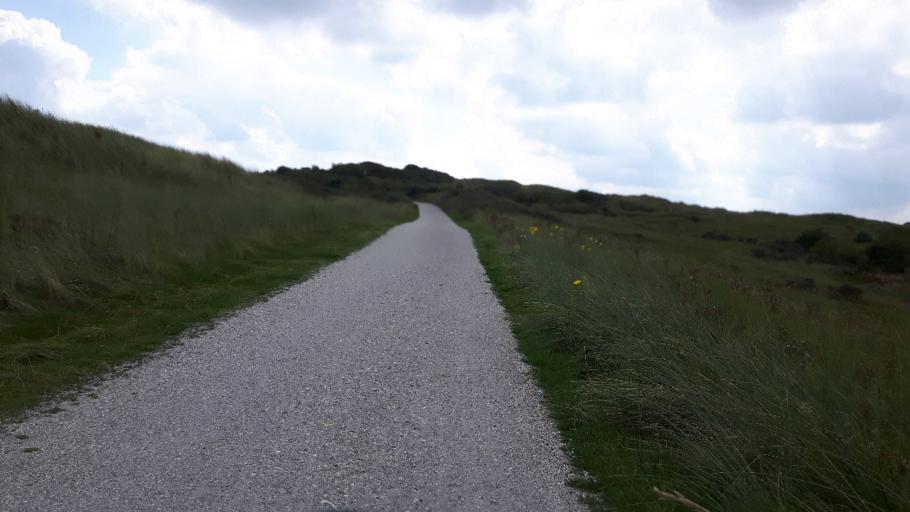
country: NL
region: Friesland
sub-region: Gemeente Dongeradeel
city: Holwerd
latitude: 53.4595
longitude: 5.9018
